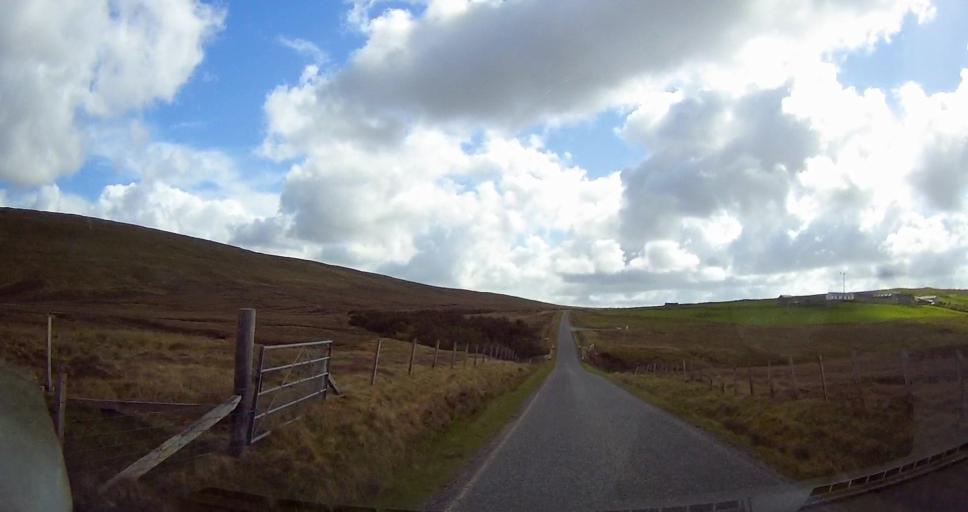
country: GB
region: Scotland
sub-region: Shetland Islands
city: Lerwick
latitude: 60.5118
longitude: -1.3855
